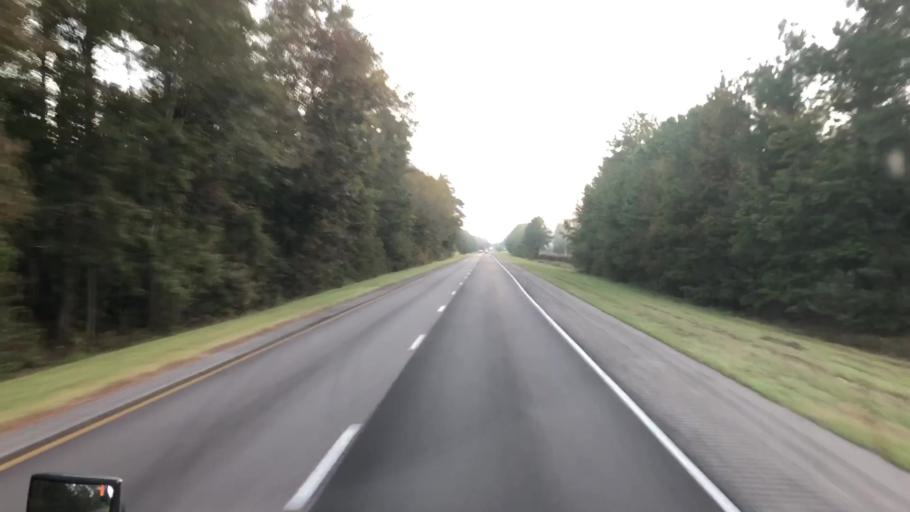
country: US
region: South Carolina
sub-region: Clarendon County
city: Manning
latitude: 33.5824
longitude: -80.3668
